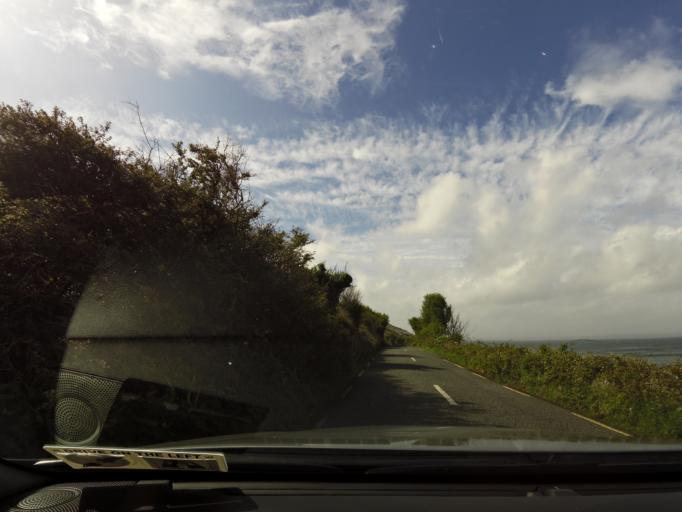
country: IE
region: Connaught
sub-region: County Galway
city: Bearna
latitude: 53.1442
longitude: -9.2337
